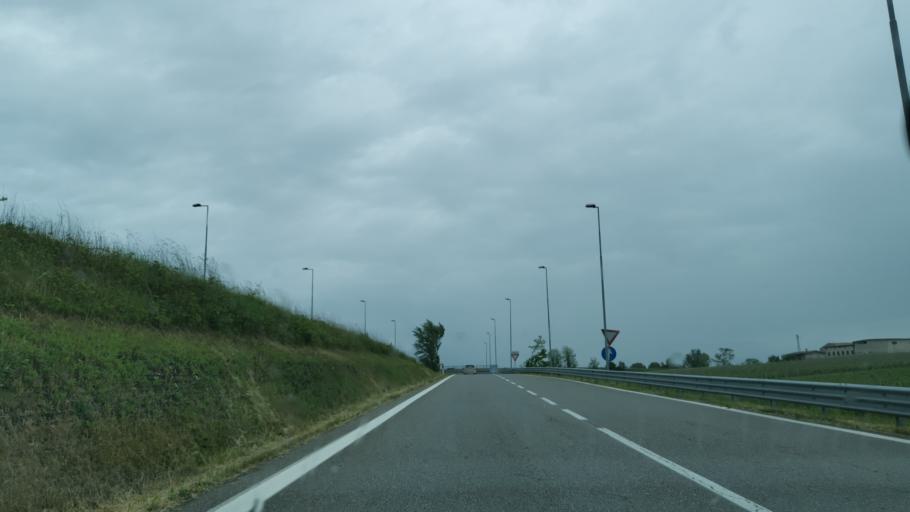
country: IT
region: Veneto
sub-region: Provincia di Verona
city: Castelnuovo del Garda
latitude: 45.4389
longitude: 10.7435
